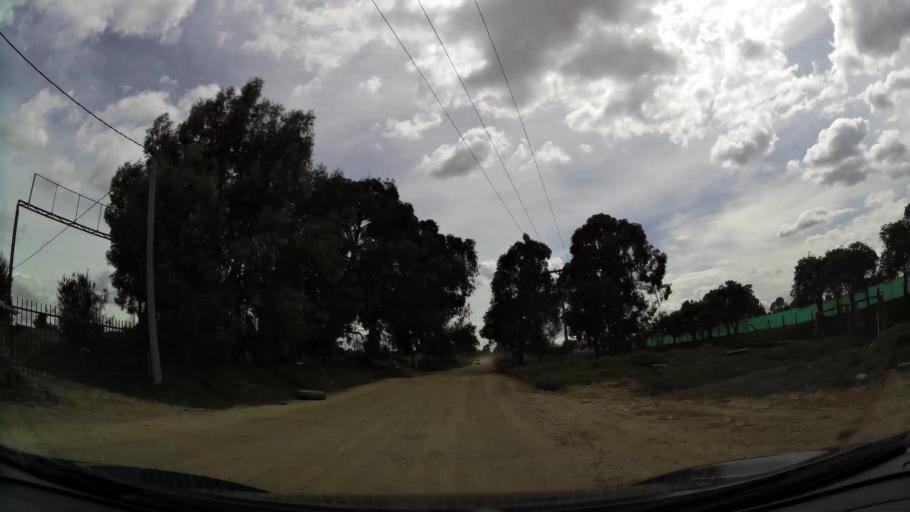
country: CO
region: Cundinamarca
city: Funza
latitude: 4.7223
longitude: -74.1655
